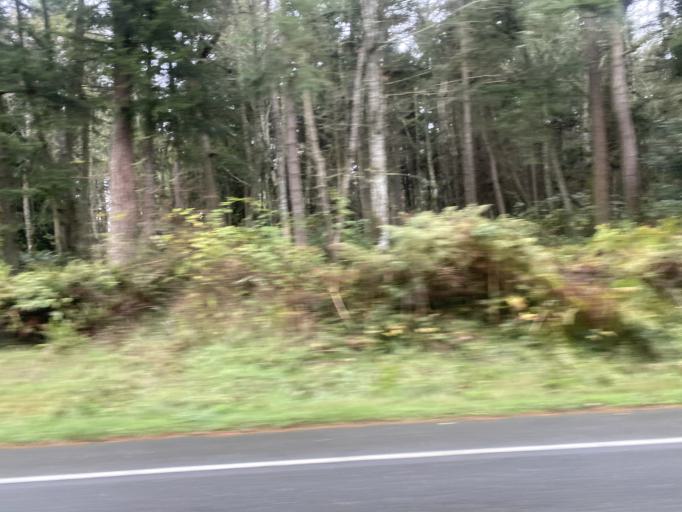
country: US
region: Washington
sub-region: Island County
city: Freeland
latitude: 48.0514
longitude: -122.5068
